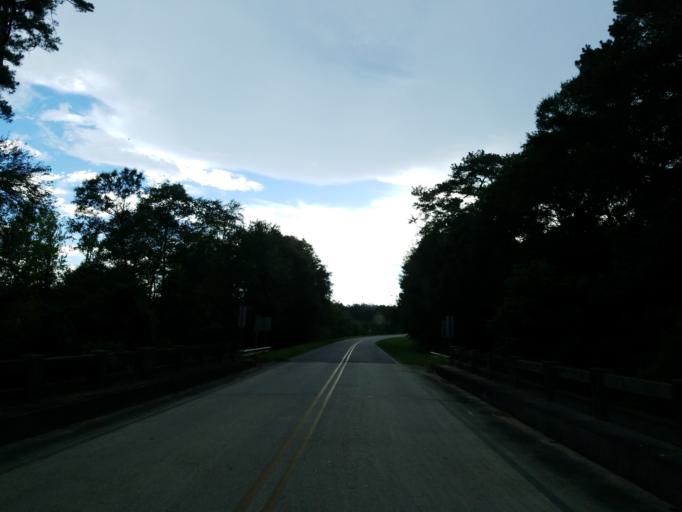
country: US
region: Georgia
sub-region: Cook County
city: Sparks
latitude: 31.2551
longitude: -83.5137
